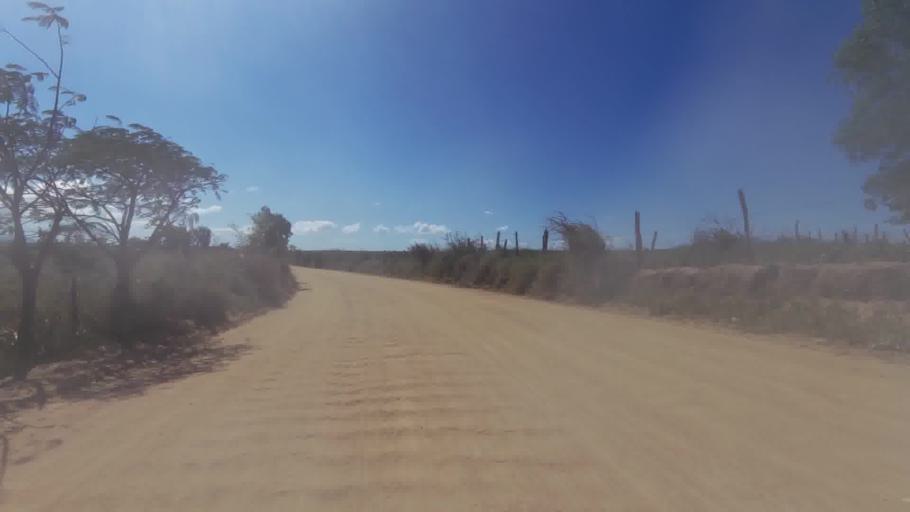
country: BR
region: Espirito Santo
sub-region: Marataizes
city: Marataizes
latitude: -21.1439
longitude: -40.9831
